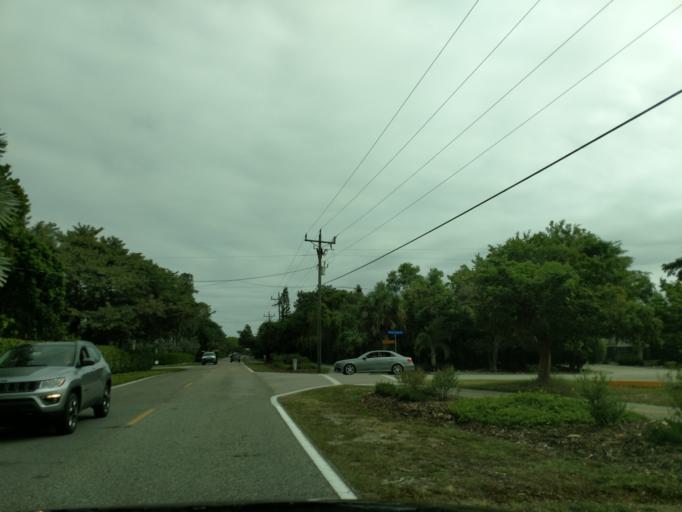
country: US
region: Florida
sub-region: Lee County
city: Sanibel
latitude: 26.4484
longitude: -82.0345
